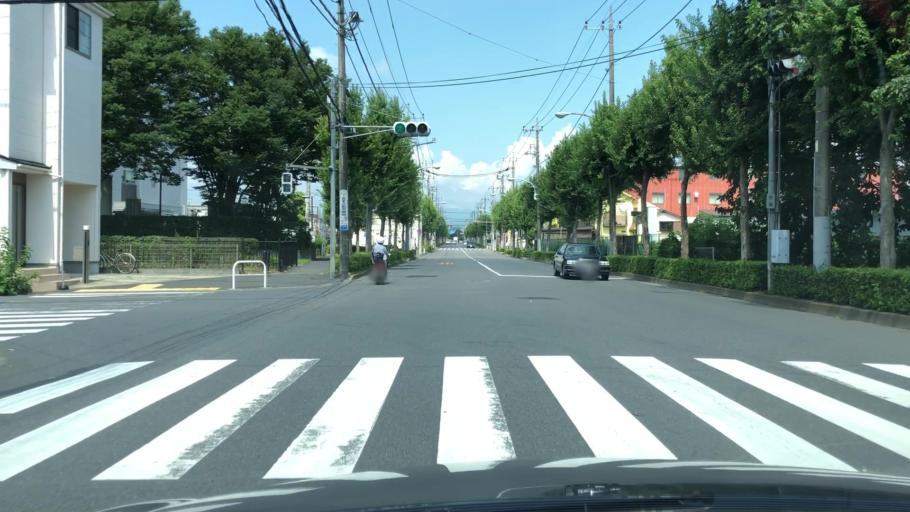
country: JP
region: Tokyo
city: Hino
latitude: 35.6878
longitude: 139.3759
